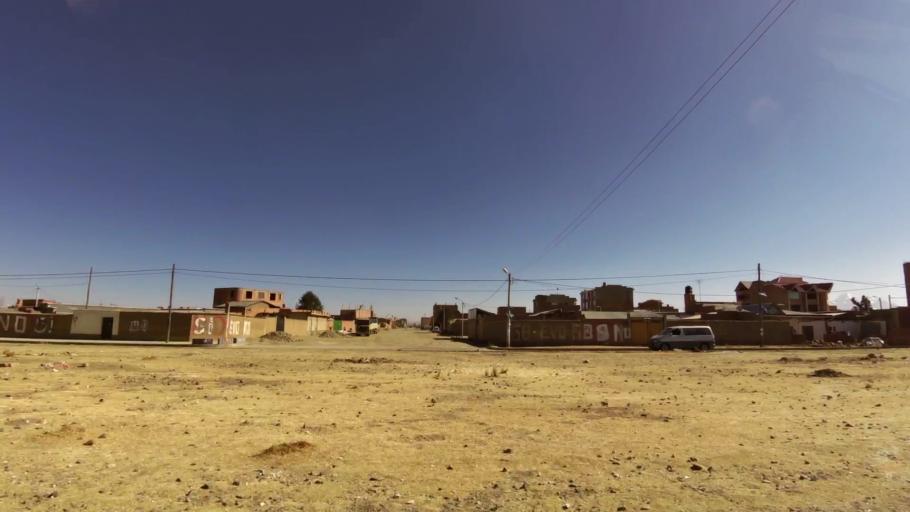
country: BO
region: La Paz
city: La Paz
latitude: -16.5320
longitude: -68.2129
